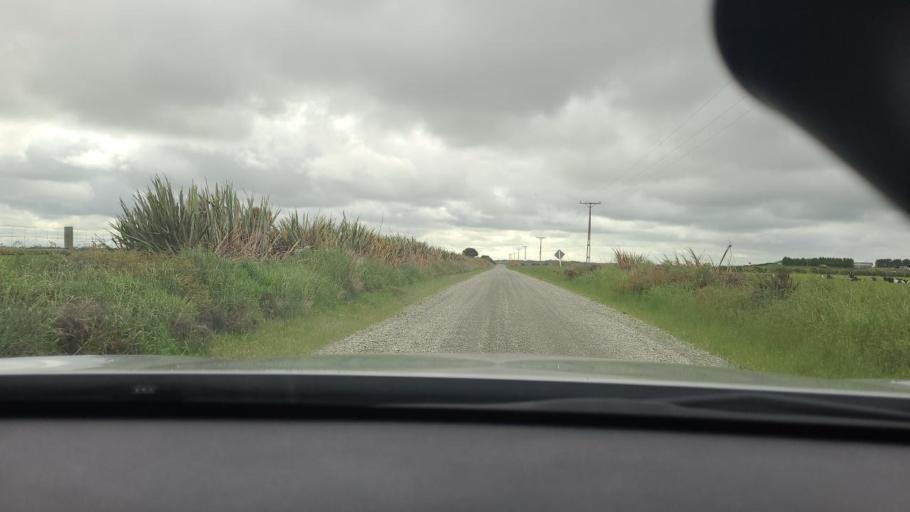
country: NZ
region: Southland
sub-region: Invercargill City
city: Invercargill
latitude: -46.3507
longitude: 168.1967
